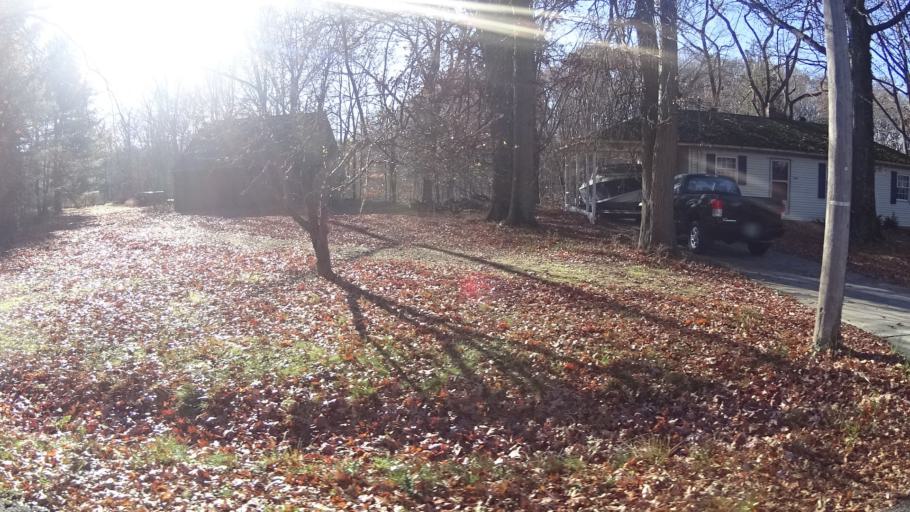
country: US
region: Ohio
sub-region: Lorain County
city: Sheffield Lake
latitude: 41.4646
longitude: -82.0913
